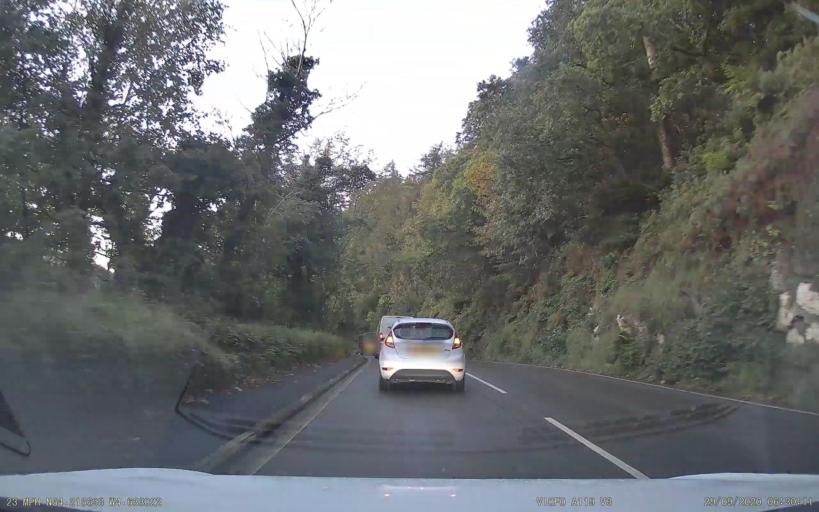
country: IM
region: Castletown
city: Castletown
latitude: 54.2157
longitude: -4.6330
